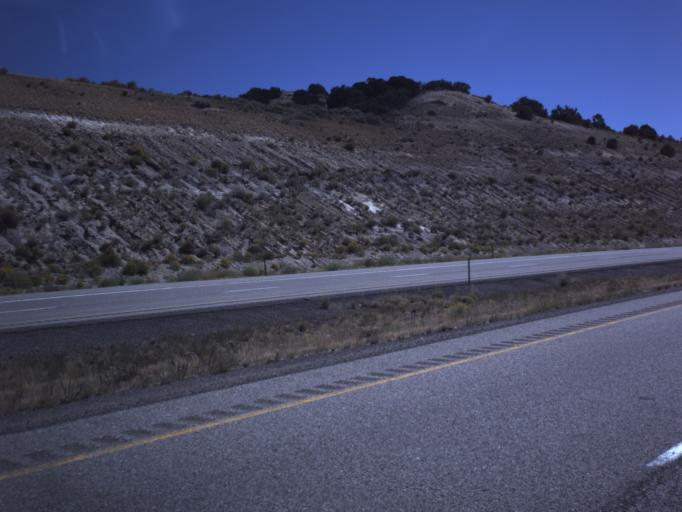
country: US
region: Utah
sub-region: Wayne County
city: Loa
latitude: 38.7820
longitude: -111.4876
